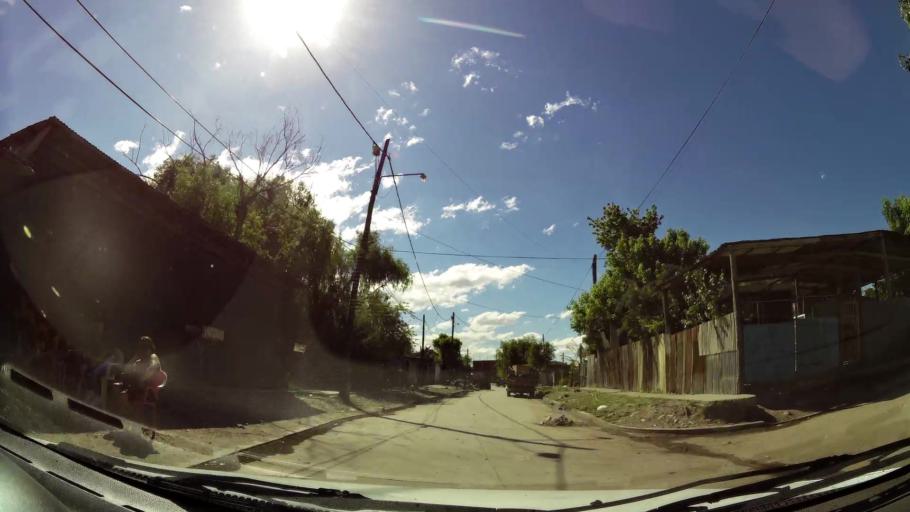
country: AR
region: Buenos Aires
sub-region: Partido de Tigre
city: Tigre
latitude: -34.5073
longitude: -58.5877
